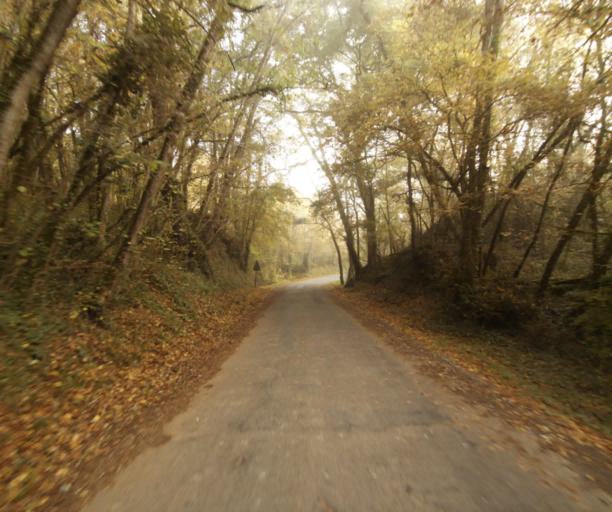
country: FR
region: Midi-Pyrenees
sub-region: Departement de la Haute-Garonne
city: Villemur-sur-Tarn
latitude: 43.8879
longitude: 1.4908
